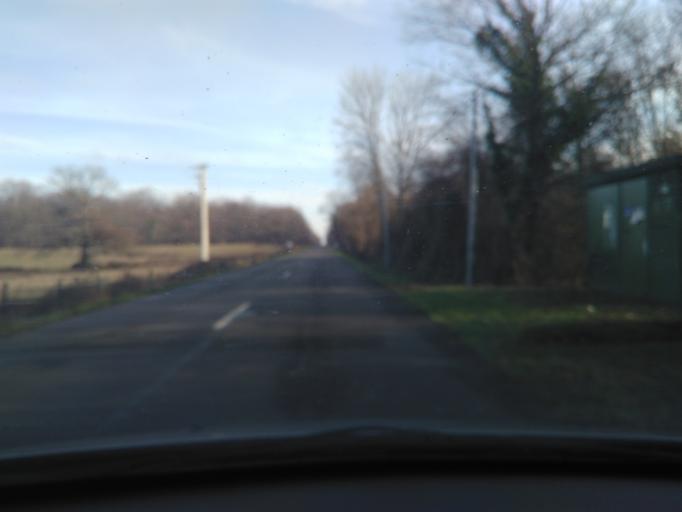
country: FR
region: Bourgogne
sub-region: Departement de la Nievre
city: Dornes
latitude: 46.7760
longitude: 3.2814
